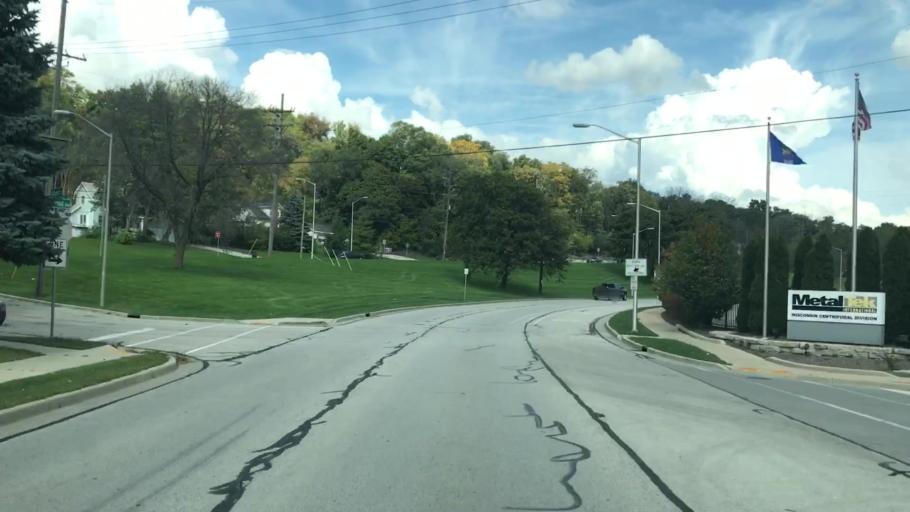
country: US
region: Wisconsin
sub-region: Waukesha County
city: Waukesha
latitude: 43.0177
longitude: -88.2294
